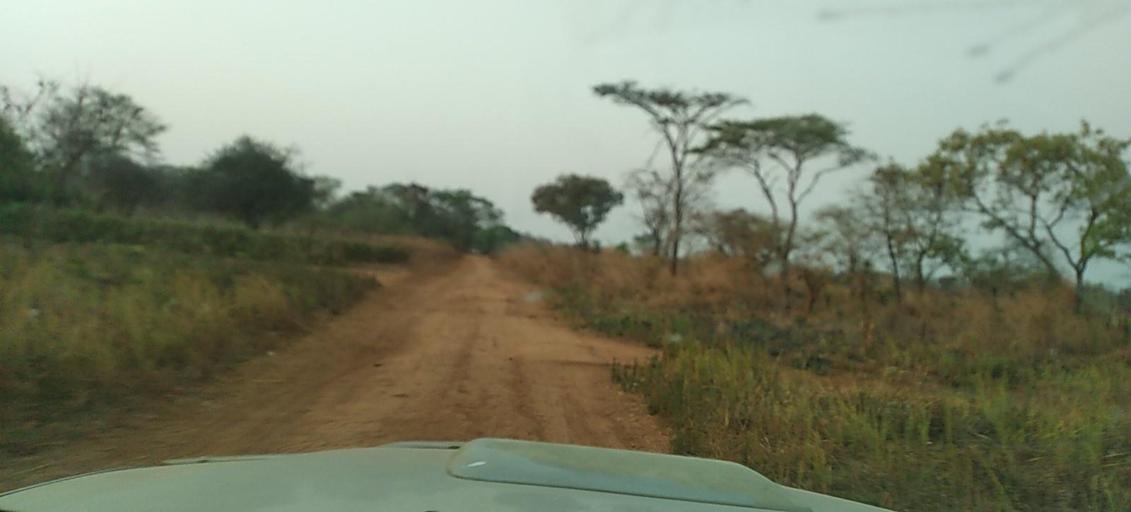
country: ZM
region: North-Western
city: Kasempa
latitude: -13.0655
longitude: 26.3817
